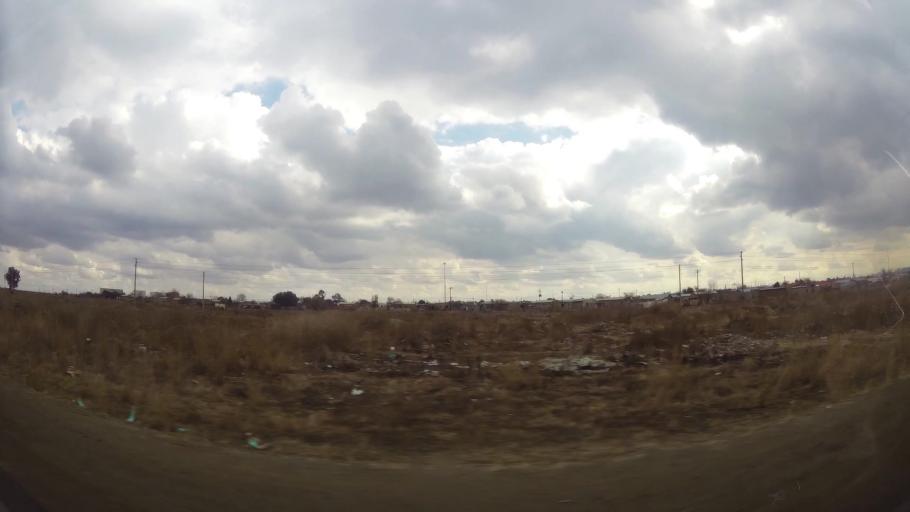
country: ZA
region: Orange Free State
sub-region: Fezile Dabi District Municipality
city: Sasolburg
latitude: -26.8604
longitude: 27.8881
